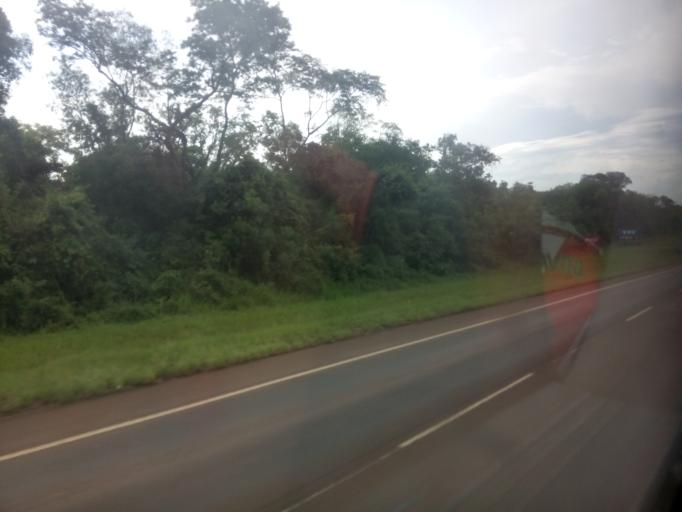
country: AR
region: Misiones
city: Santa Ana
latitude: -27.4007
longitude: -55.6024
